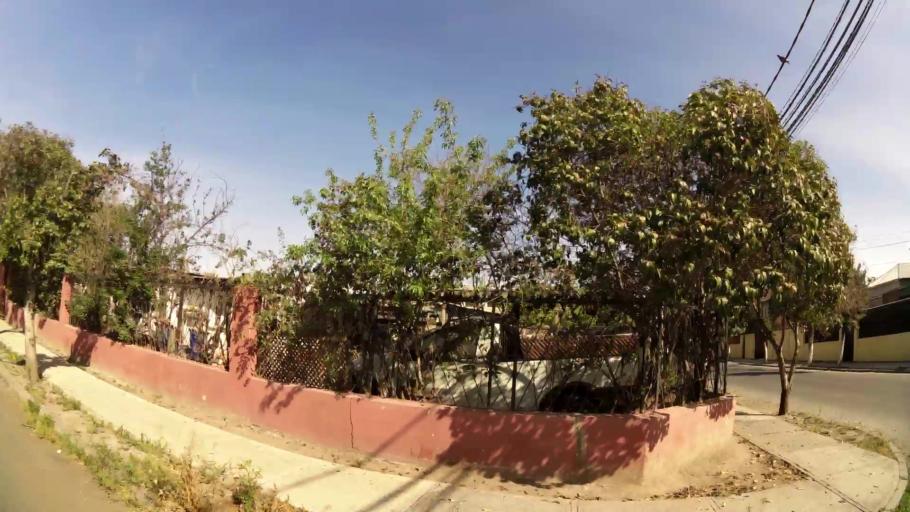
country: CL
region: Santiago Metropolitan
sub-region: Provincia de Santiago
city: La Pintana
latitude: -33.5311
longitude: -70.5913
